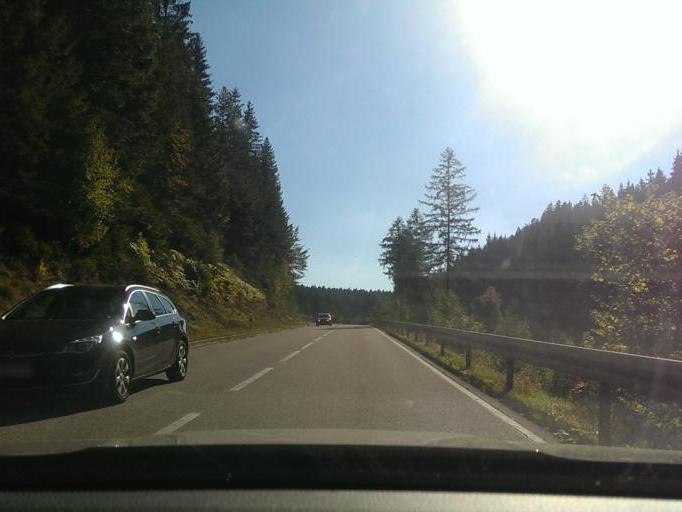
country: DE
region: Baden-Wuerttemberg
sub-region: Karlsruhe Region
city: Simmersfeld
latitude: 48.6524
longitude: 8.5162
